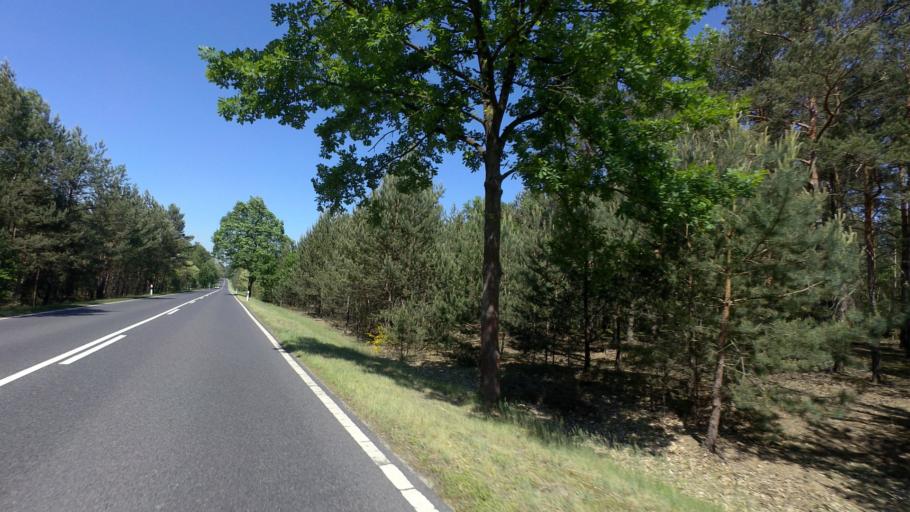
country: DE
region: Brandenburg
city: Lieberose
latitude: 51.9506
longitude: 14.3332
